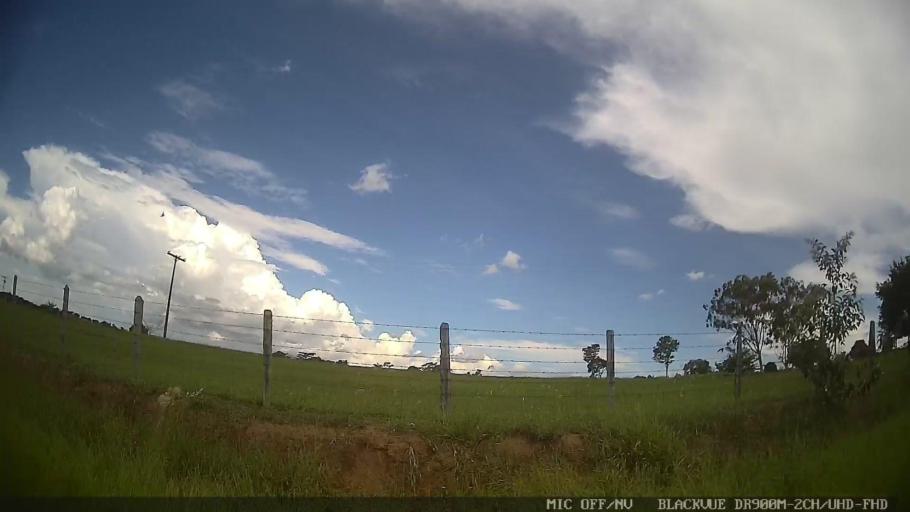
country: BR
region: Sao Paulo
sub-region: Conchas
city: Conchas
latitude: -22.9925
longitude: -47.9980
